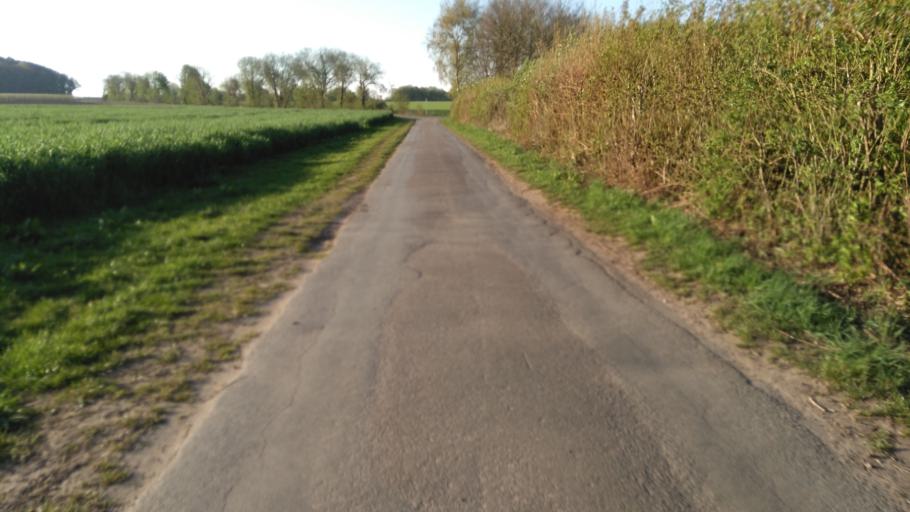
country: DE
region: Lower Saxony
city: Bliedersdorf
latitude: 53.4758
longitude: 9.5784
